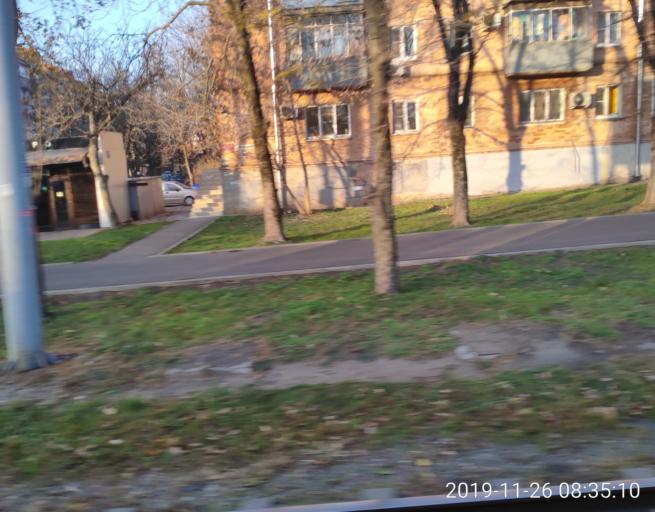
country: RU
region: Krasnodarskiy
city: Krasnodar
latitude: 45.0548
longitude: 38.9895
